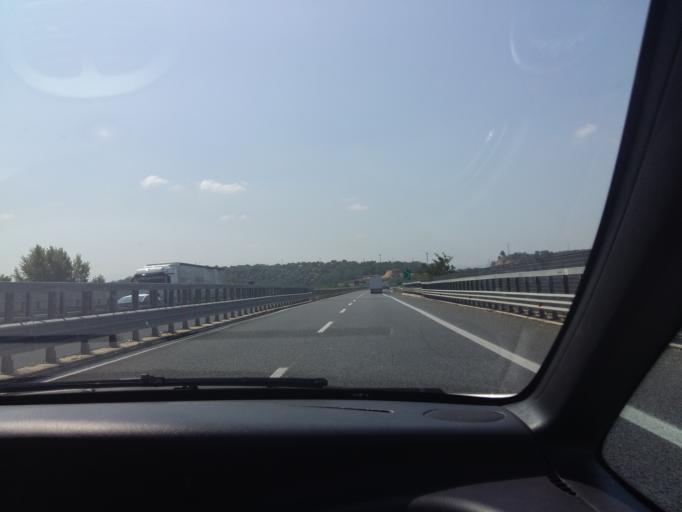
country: IT
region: Calabria
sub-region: Provincia di Reggio Calabria
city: Rosarno
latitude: 38.4923
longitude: 16.0103
